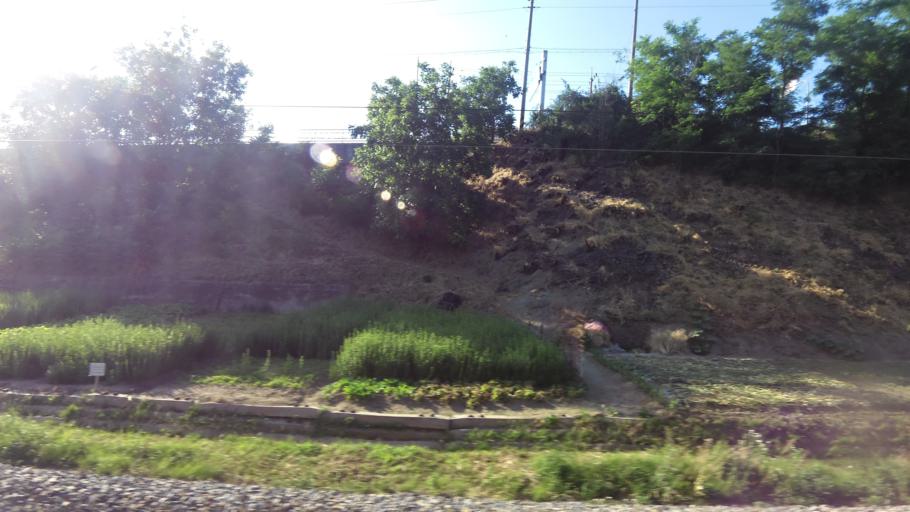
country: KR
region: Gyeongsangbuk-do
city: Gimcheon
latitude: 36.1177
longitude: 128.1412
